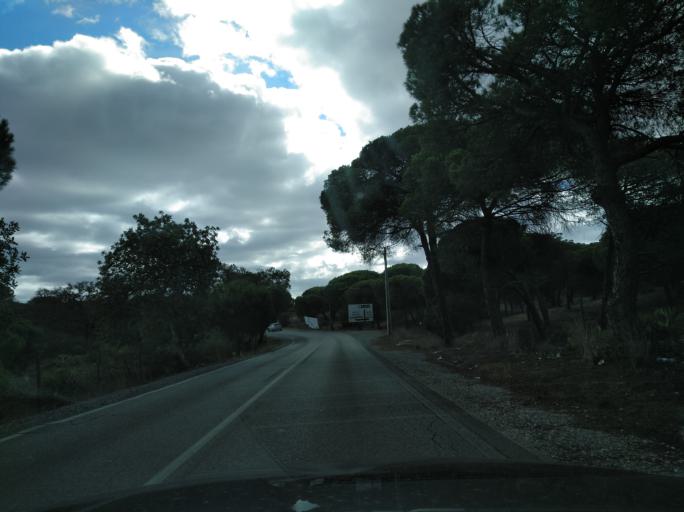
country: PT
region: Faro
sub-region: Vila Real de Santo Antonio
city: Monte Gordo
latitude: 37.1863
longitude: -7.4845
